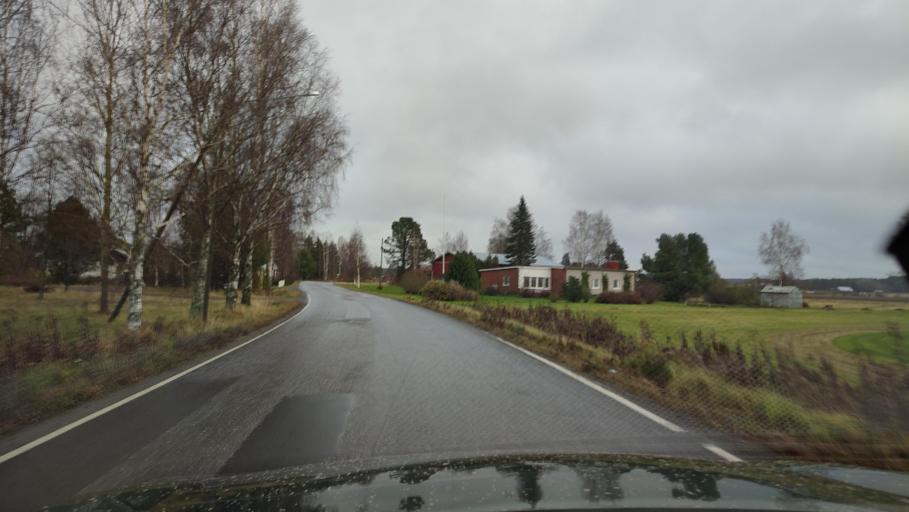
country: FI
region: Ostrobothnia
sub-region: Sydosterbotten
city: Kristinestad
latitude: 62.3056
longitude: 21.4615
